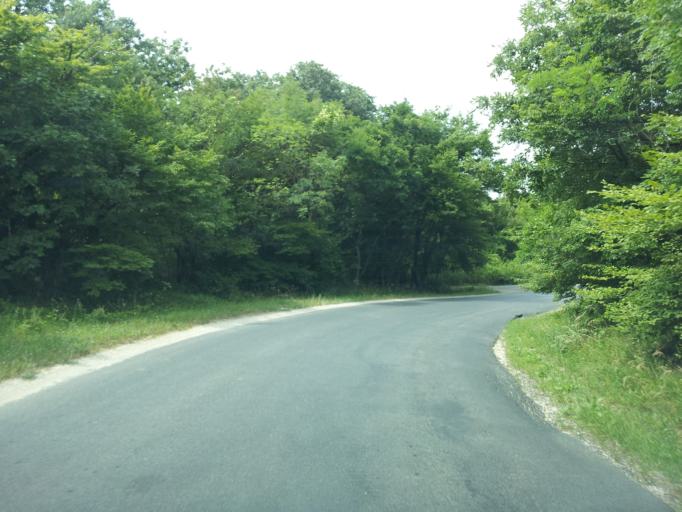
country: HU
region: Veszprem
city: Zanka
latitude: 46.9354
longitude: 17.7005
